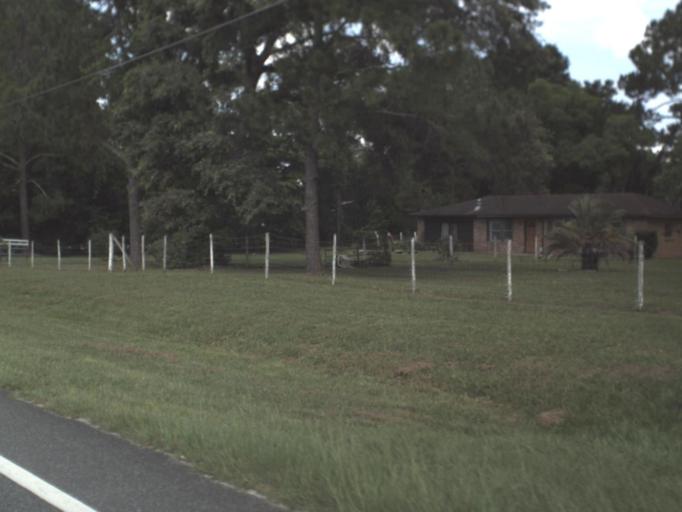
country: US
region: Florida
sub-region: Alachua County
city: Archer
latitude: 29.5643
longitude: -82.4780
